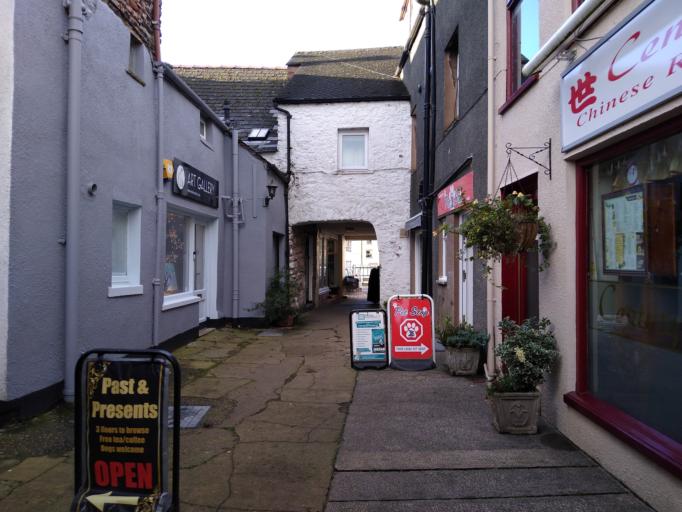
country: GB
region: England
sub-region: Cumbria
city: Kirkby Stephen
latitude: 54.4734
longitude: -2.3478
